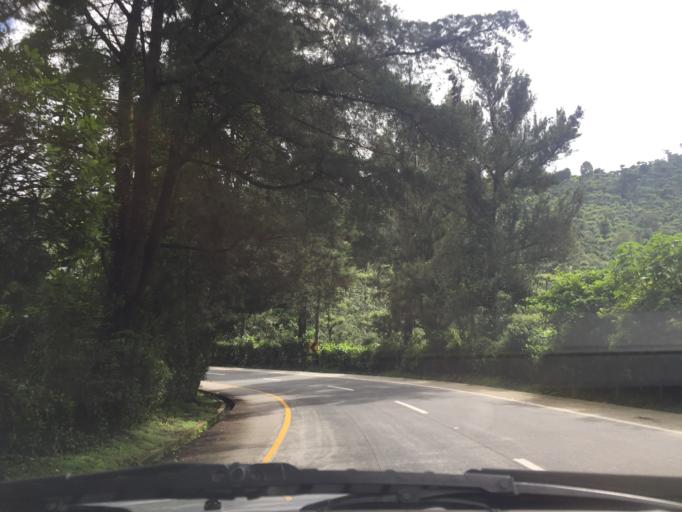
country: GT
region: Sacatepequez
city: Santa Lucia Milpas Altas
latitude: 14.5580
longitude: -90.7030
